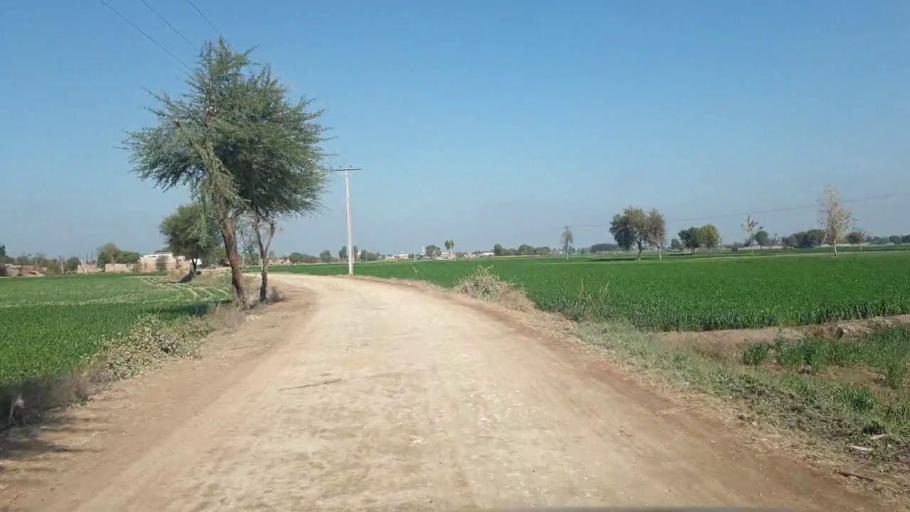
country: PK
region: Sindh
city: Bhit Shah
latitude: 25.8874
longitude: 68.5267
